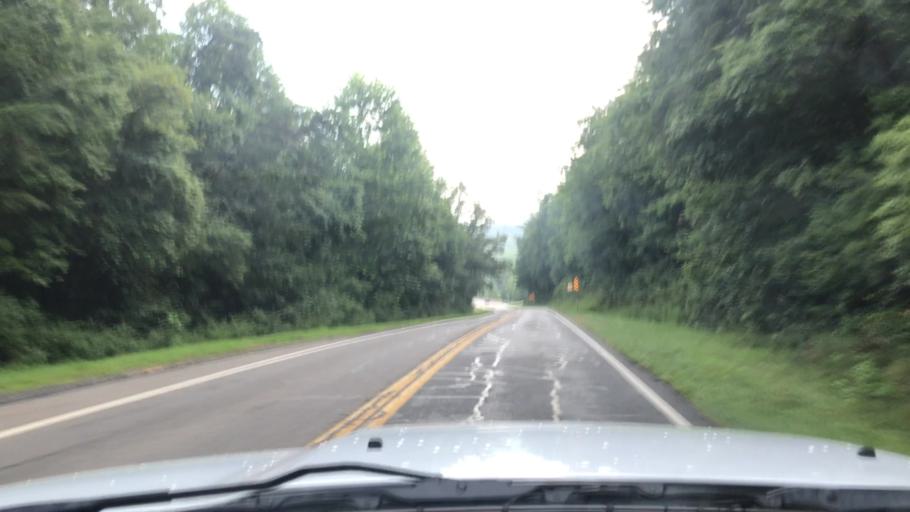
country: US
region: Georgia
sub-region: Fannin County
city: Blue Ridge
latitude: 34.9207
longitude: -84.2720
